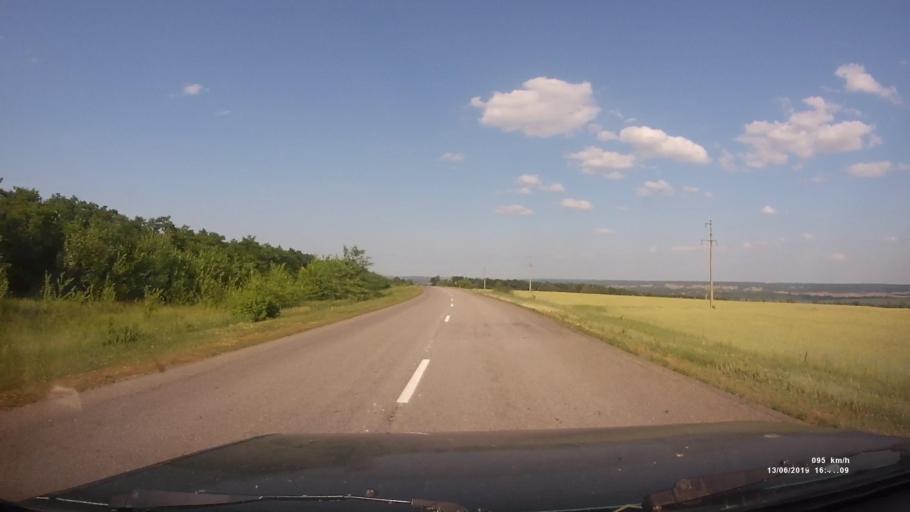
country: RU
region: Rostov
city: Kazanskaya
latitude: 49.9336
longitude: 41.3778
